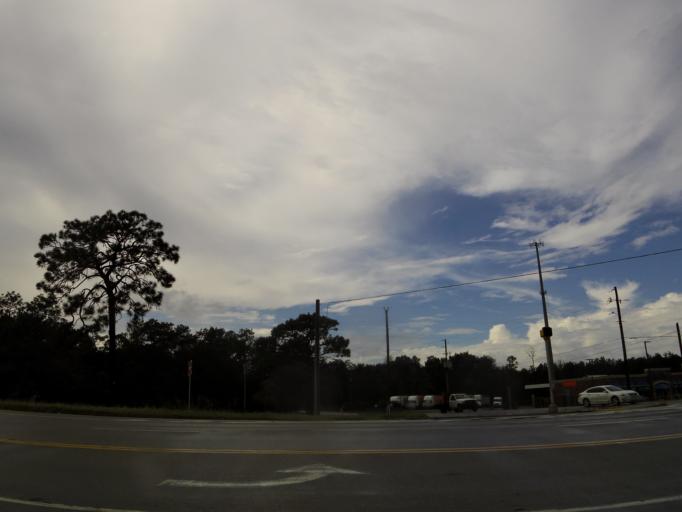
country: US
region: Georgia
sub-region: Wayne County
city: Jesup
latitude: 31.6610
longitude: -81.8486
